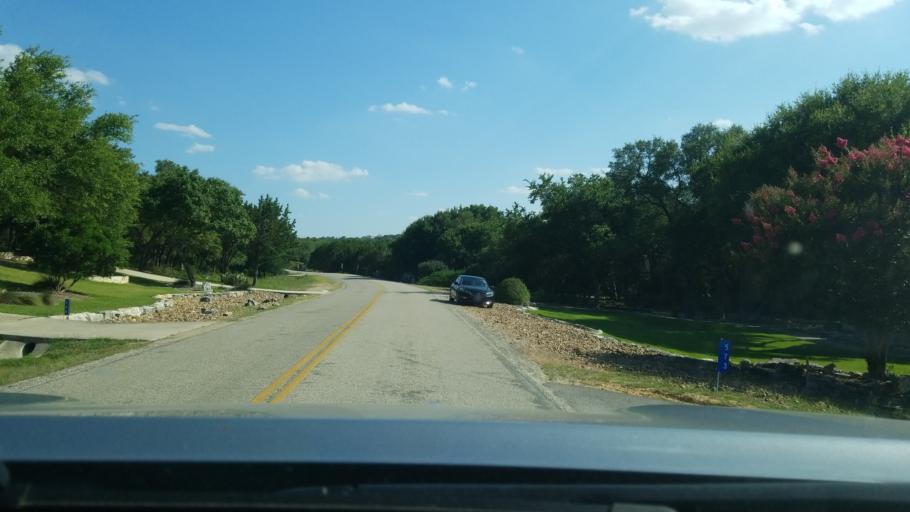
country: US
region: Texas
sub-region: Comal County
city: Bulverde
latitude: 29.8209
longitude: -98.3999
